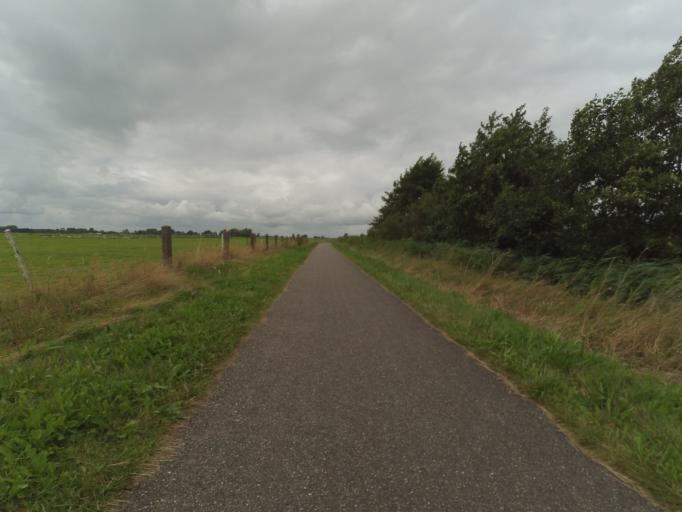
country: NL
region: Friesland
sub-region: Gemeente Kollumerland en Nieuwkruisland
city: Kollumerzwaag
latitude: 53.2890
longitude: 6.1087
